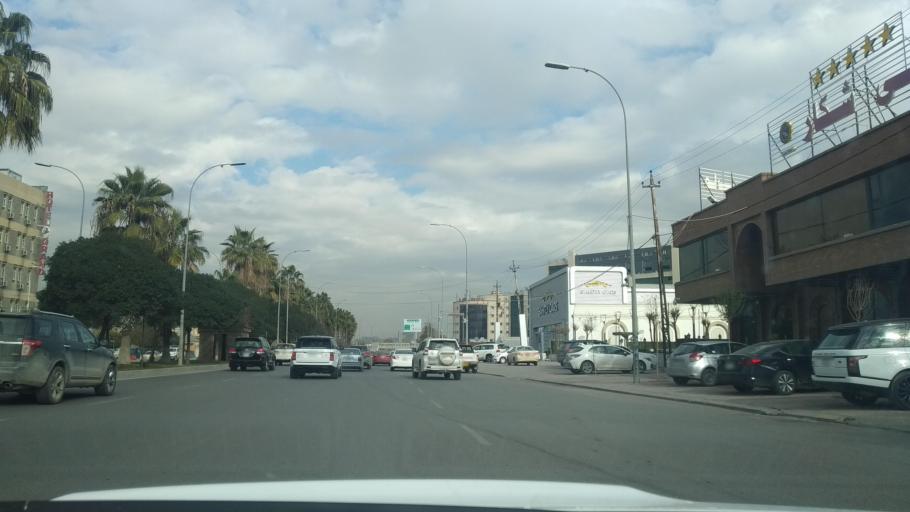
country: IQ
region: Arbil
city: Erbil
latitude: 36.1865
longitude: 43.9939
